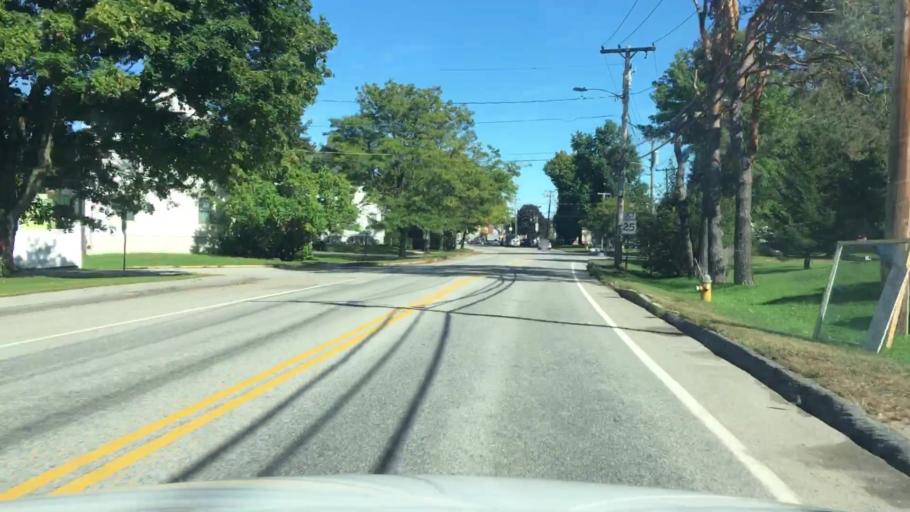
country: US
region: Maine
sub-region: Cumberland County
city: Westbrook
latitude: 43.6770
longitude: -70.3750
